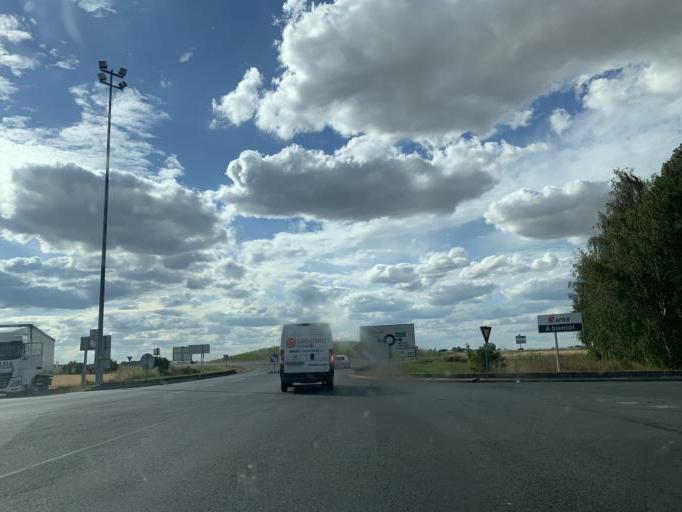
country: FR
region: Ile-de-France
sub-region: Departement de Seine-et-Marne
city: Moisenay
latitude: 48.5886
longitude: 2.7238
